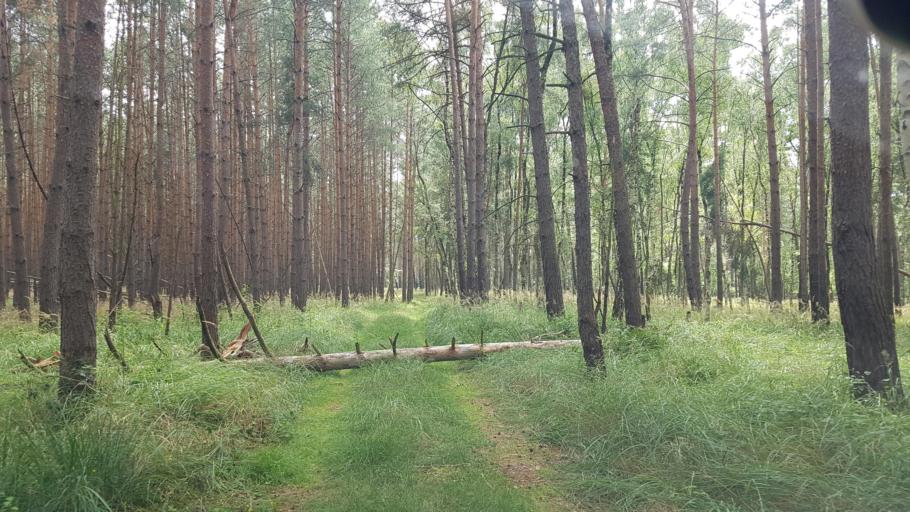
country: DE
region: Brandenburg
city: Trobitz
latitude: 51.6347
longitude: 13.4168
